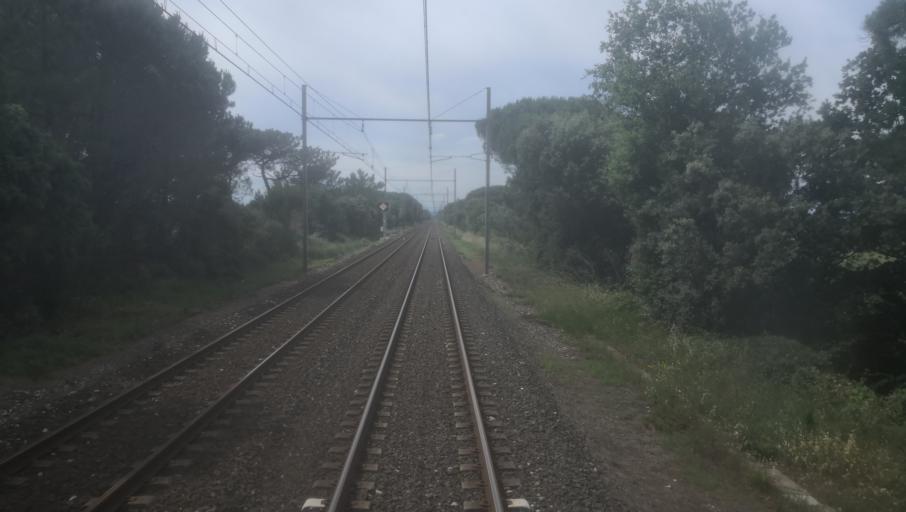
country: FR
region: Languedoc-Roussillon
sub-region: Departement du Gard
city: Redessan
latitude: 43.8002
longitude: 4.5286
